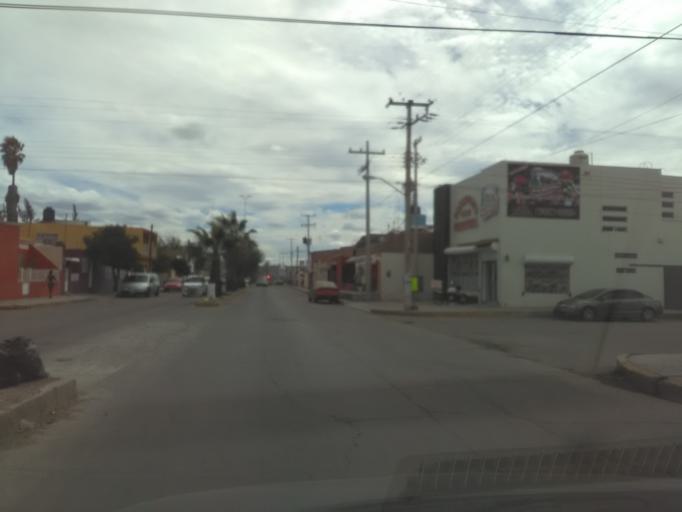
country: MX
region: Durango
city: Victoria de Durango
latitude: 24.0472
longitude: -104.6843
